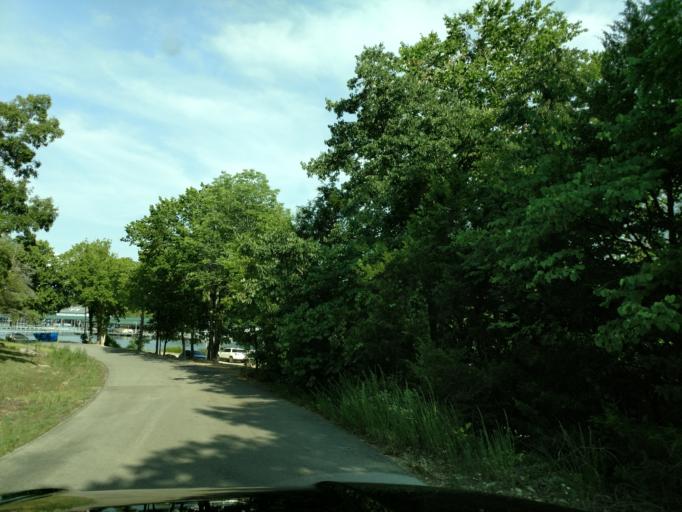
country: US
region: Missouri
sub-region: Barry County
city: Shell Knob
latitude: 36.5952
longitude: -93.5516
